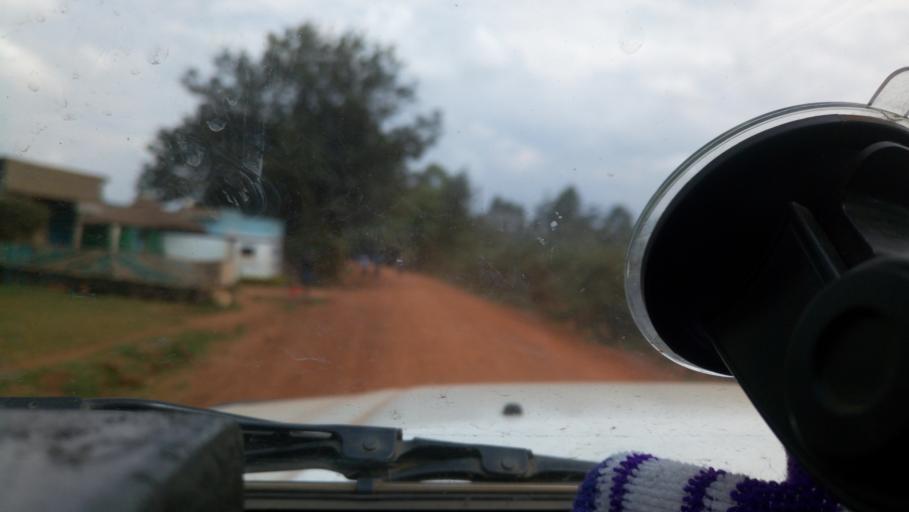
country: KE
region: Kericho
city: Litein
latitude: -0.6074
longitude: 35.1382
